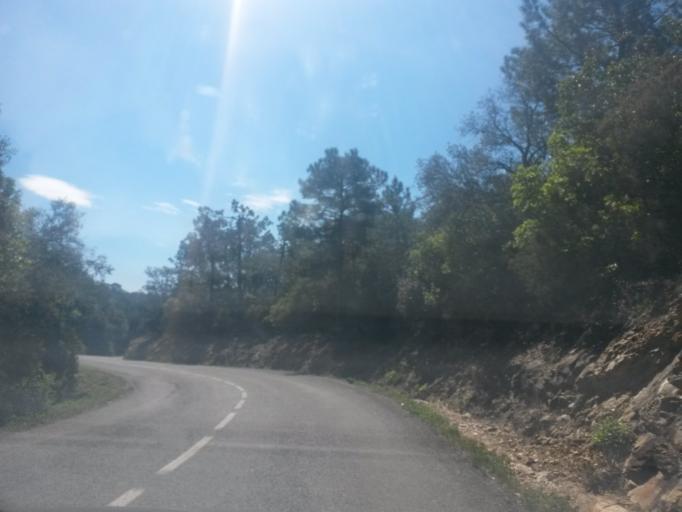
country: ES
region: Catalonia
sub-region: Provincia de Girona
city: Juia
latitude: 41.9826
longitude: 2.9241
